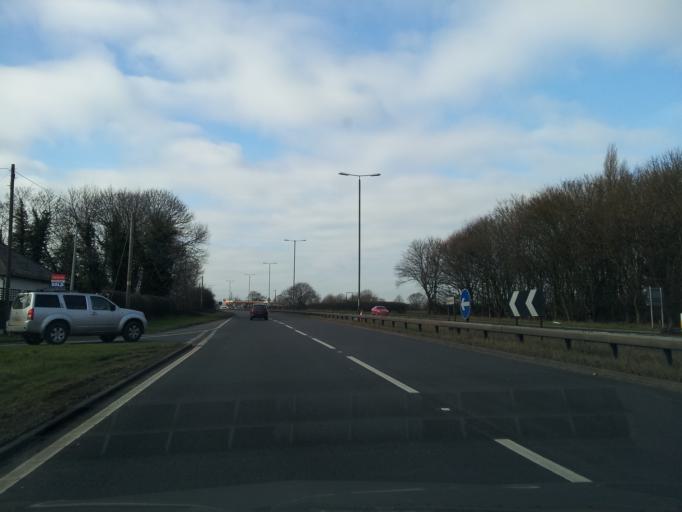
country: GB
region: England
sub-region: Derbyshire
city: Borrowash
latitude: 52.9134
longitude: -1.3771
